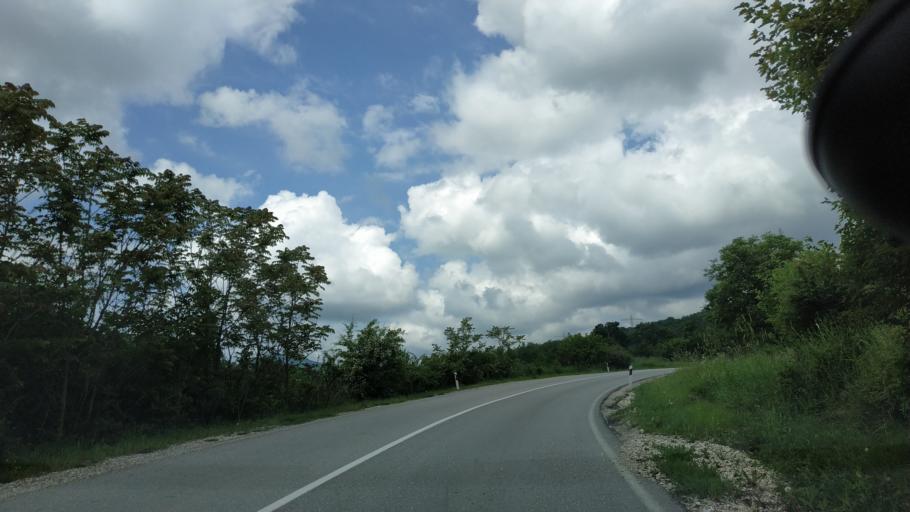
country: RS
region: Central Serbia
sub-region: Borski Okrug
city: Bor
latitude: 44.0581
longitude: 22.0537
